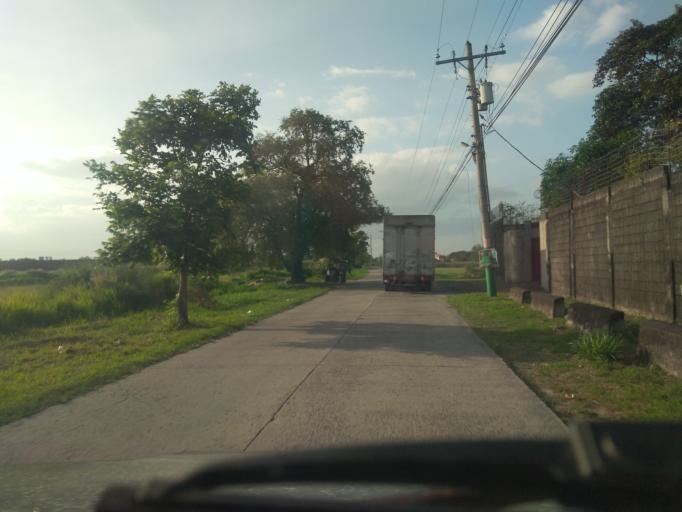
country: PH
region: Central Luzon
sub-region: Province of Pampanga
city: Malino
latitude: 15.1098
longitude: 120.6683
